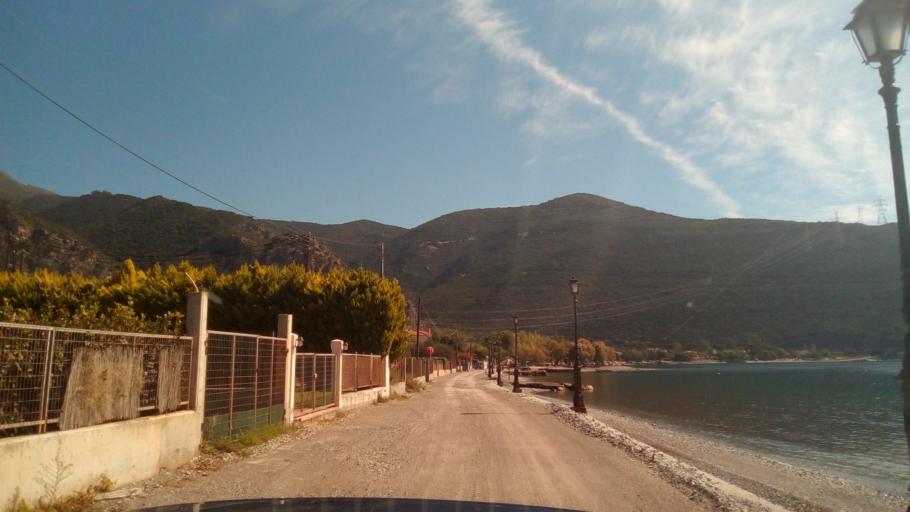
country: GR
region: West Greece
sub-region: Nomos Achaias
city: Selianitika
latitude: 38.3679
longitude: 22.1201
